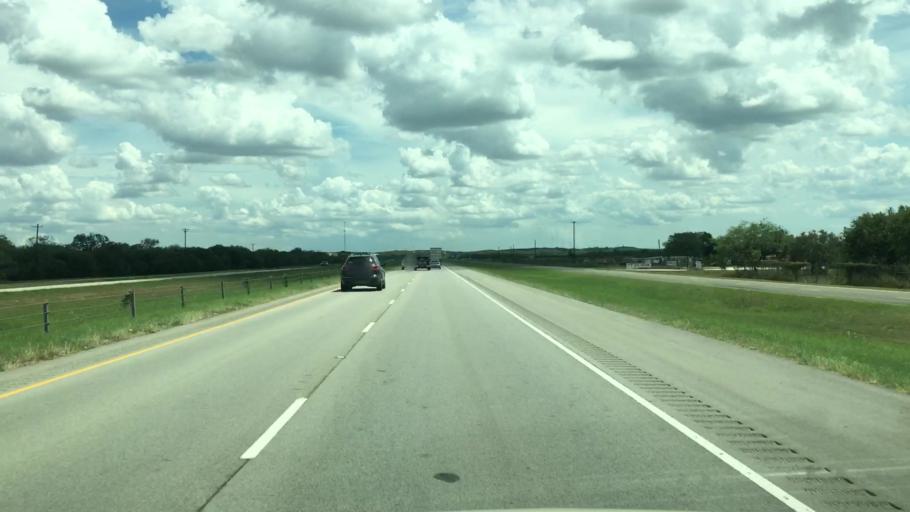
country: US
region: Texas
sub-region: Live Oak County
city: George West
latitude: 28.2726
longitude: -97.9461
